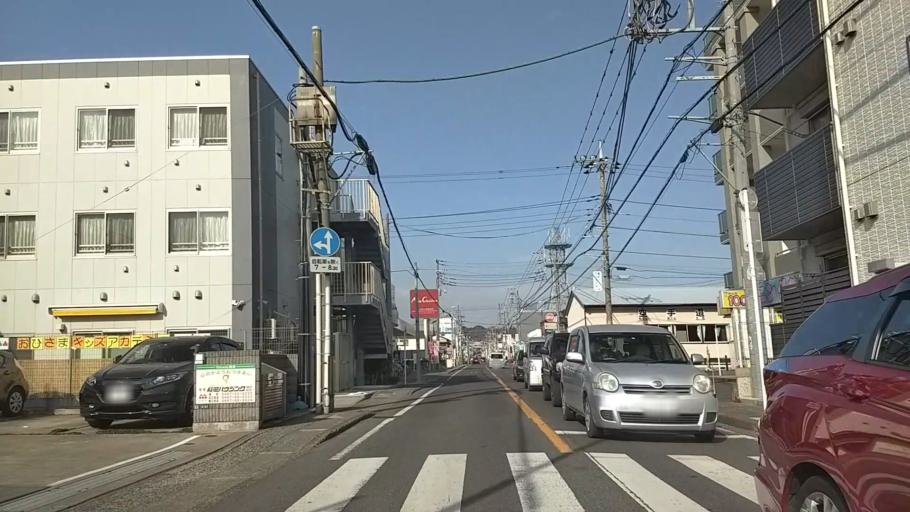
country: JP
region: Kanagawa
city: Chigasaki
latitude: 35.3440
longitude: 139.4123
